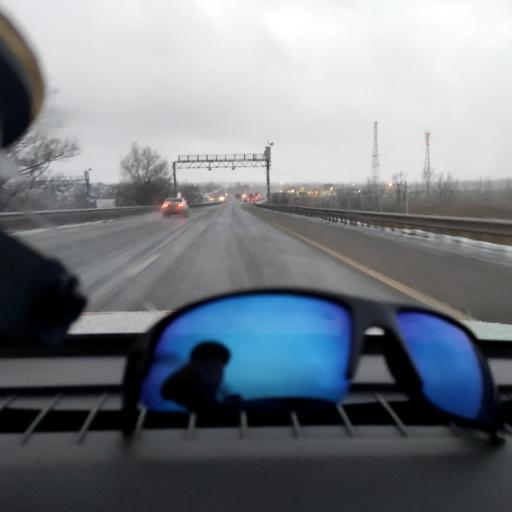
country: RU
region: Samara
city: Novosemeykino
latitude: 53.4196
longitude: 50.3313
